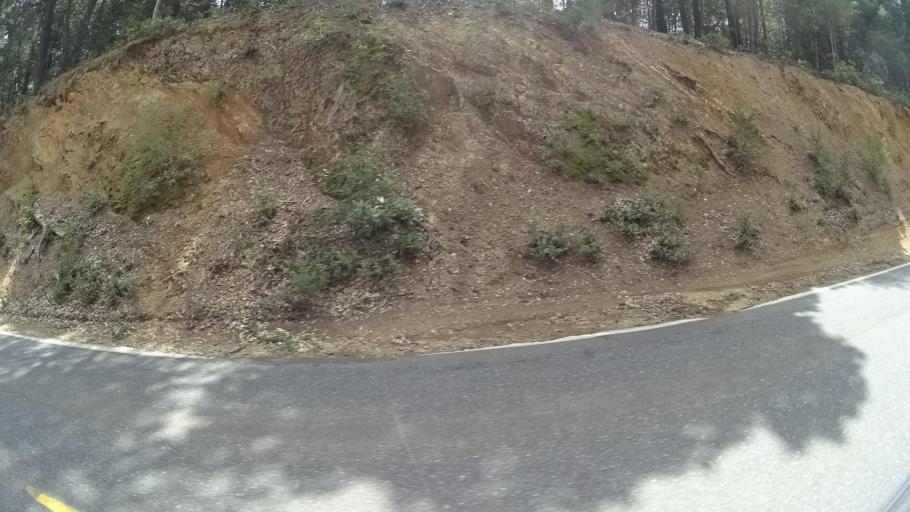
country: US
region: California
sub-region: Humboldt County
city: Redway
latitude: 40.0518
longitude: -124.0045
